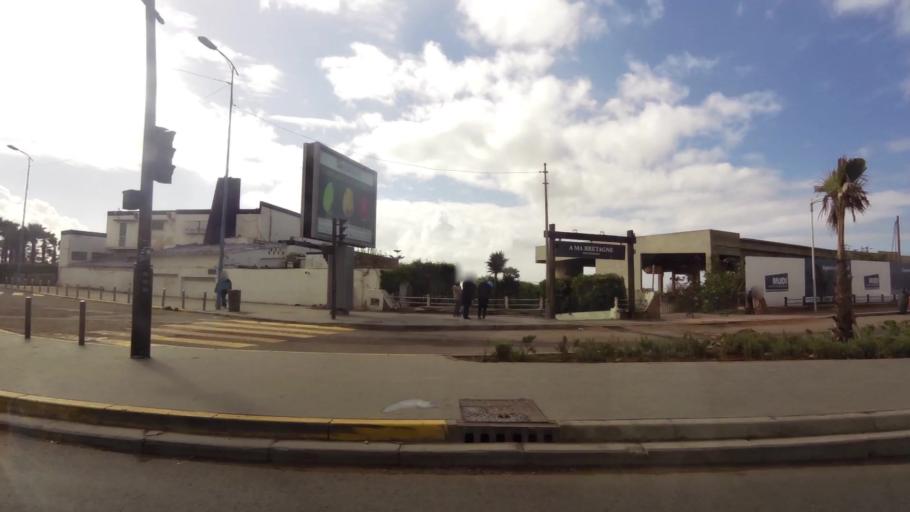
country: MA
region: Grand Casablanca
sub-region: Casablanca
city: Casablanca
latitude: 33.5780
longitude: -7.7042
